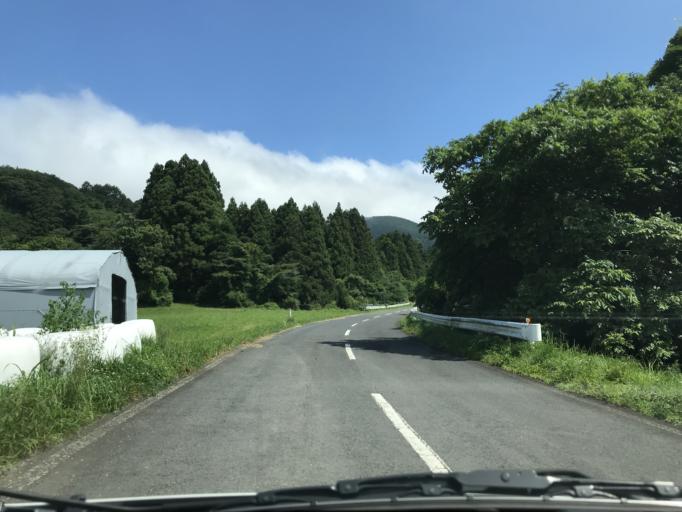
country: JP
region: Iwate
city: Ofunato
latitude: 38.9995
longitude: 141.4283
